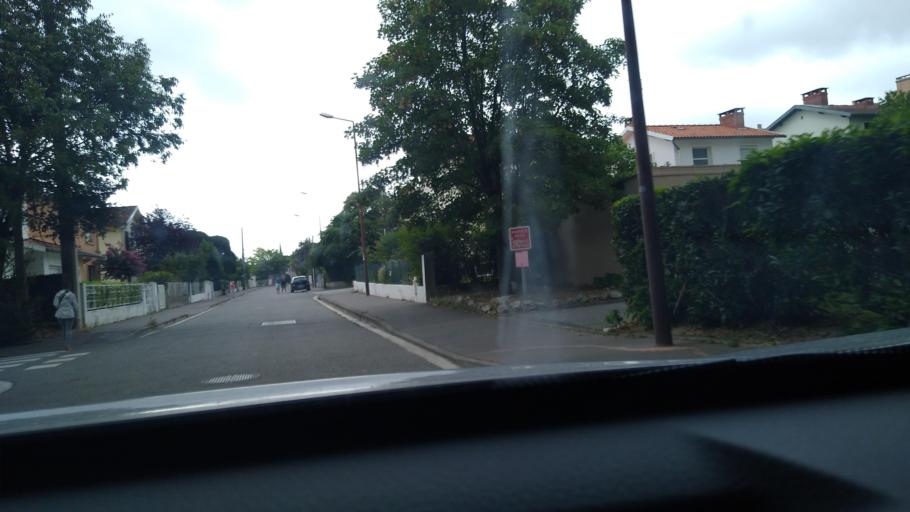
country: FR
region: Midi-Pyrenees
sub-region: Departement de la Haute-Garonne
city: Toulouse
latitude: 43.6128
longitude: 1.4706
